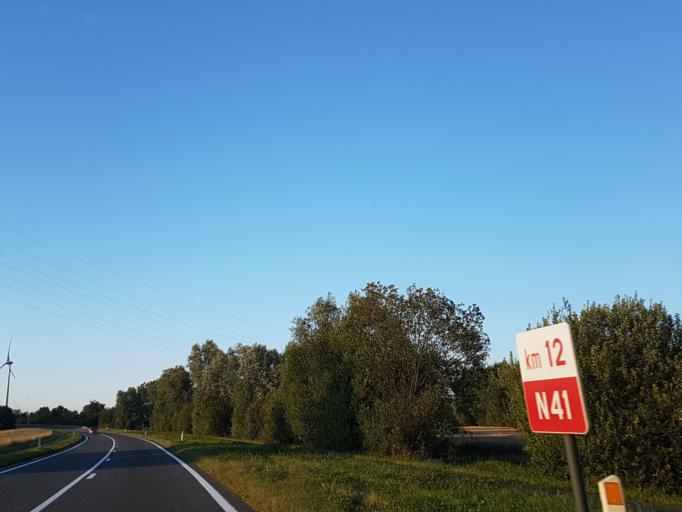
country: BE
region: Flanders
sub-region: Provincie Oost-Vlaanderen
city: Lebbeke
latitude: 51.0145
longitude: 4.1320
